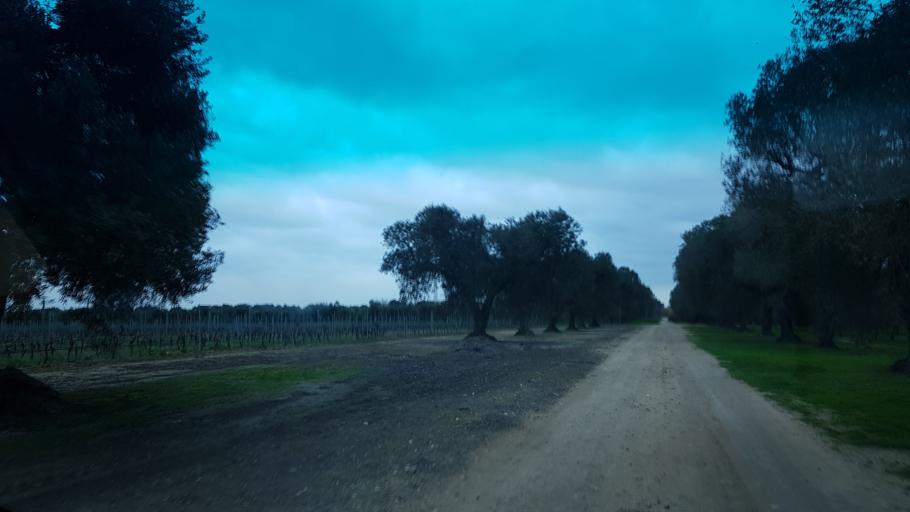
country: IT
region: Apulia
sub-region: Provincia di Brindisi
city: La Rosa
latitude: 40.5857
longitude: 17.9871
